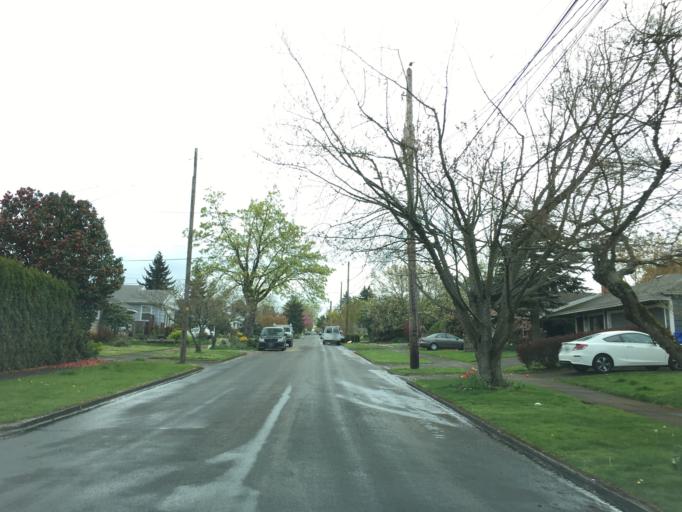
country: US
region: Oregon
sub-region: Multnomah County
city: Lents
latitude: 45.5550
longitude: -122.5902
